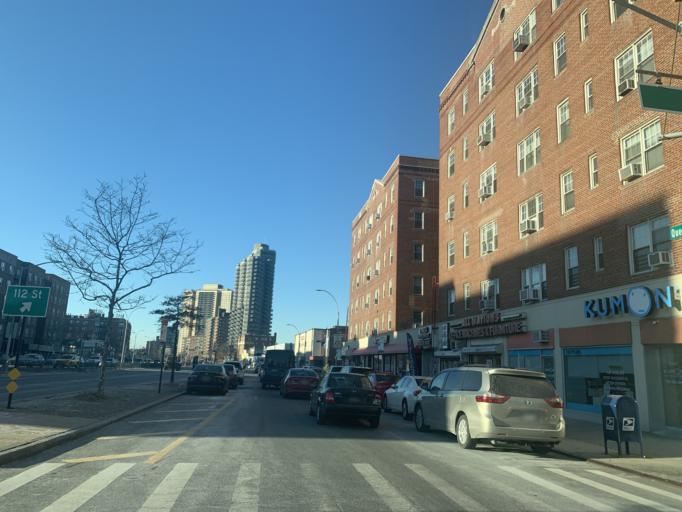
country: US
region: New York
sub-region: Queens County
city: Borough of Queens
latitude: 40.7163
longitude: -73.8334
